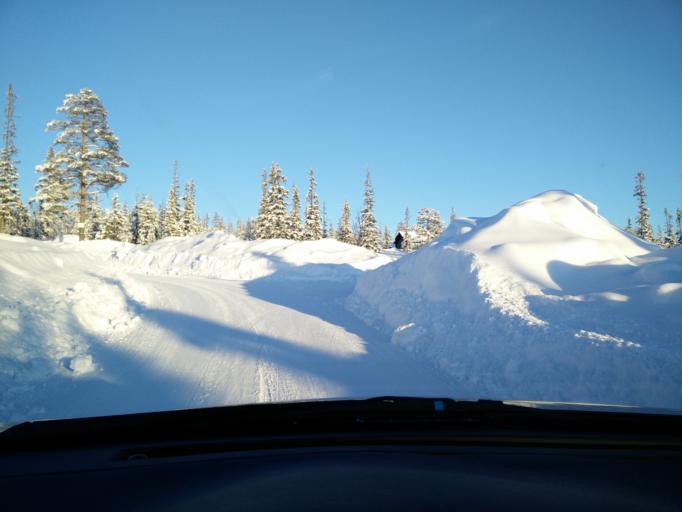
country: SE
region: Jaemtland
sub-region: Bergs Kommun
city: Hoverberg
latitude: 62.4954
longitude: 14.1249
